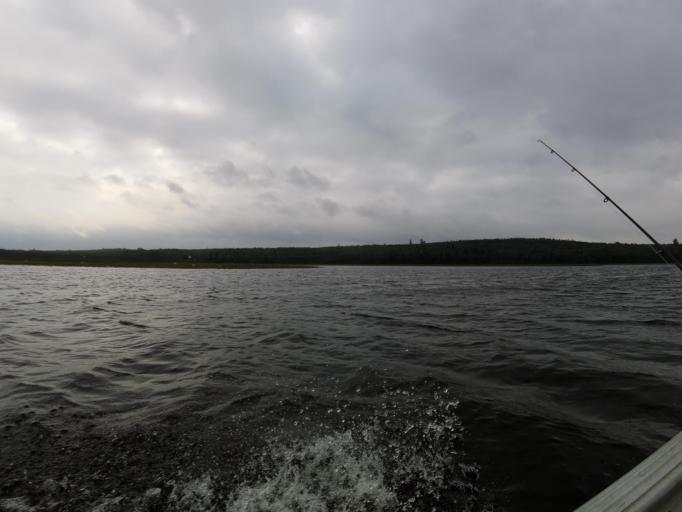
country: CA
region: Ontario
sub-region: Rainy River District
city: Atikokan
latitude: 49.5871
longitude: -91.3747
